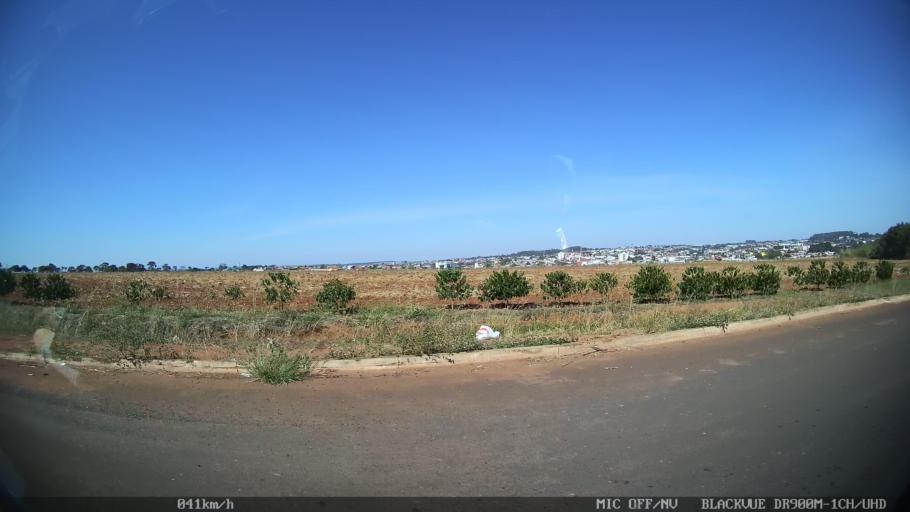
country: BR
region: Sao Paulo
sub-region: Batatais
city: Batatais
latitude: -20.8759
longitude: -47.5823
